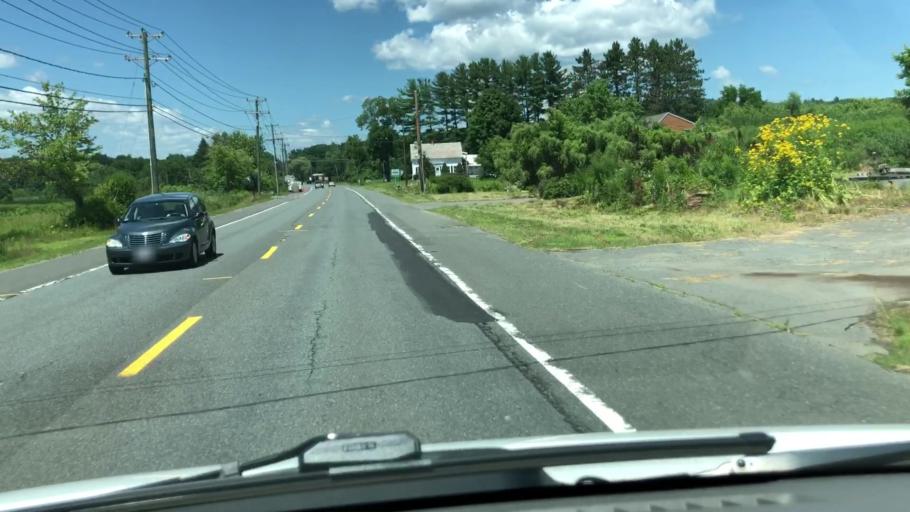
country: US
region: Massachusetts
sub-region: Hampshire County
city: North Amherst
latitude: 42.4263
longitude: -72.5395
